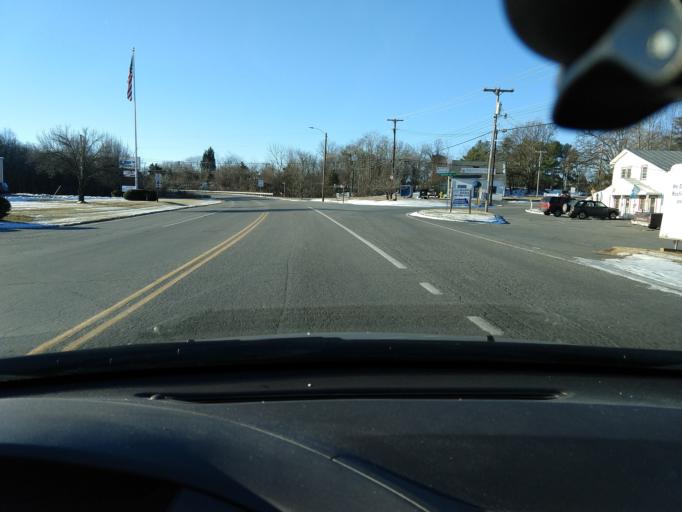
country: US
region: Virginia
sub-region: City of Bedford
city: Bedford
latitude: 37.3151
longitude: -79.5380
